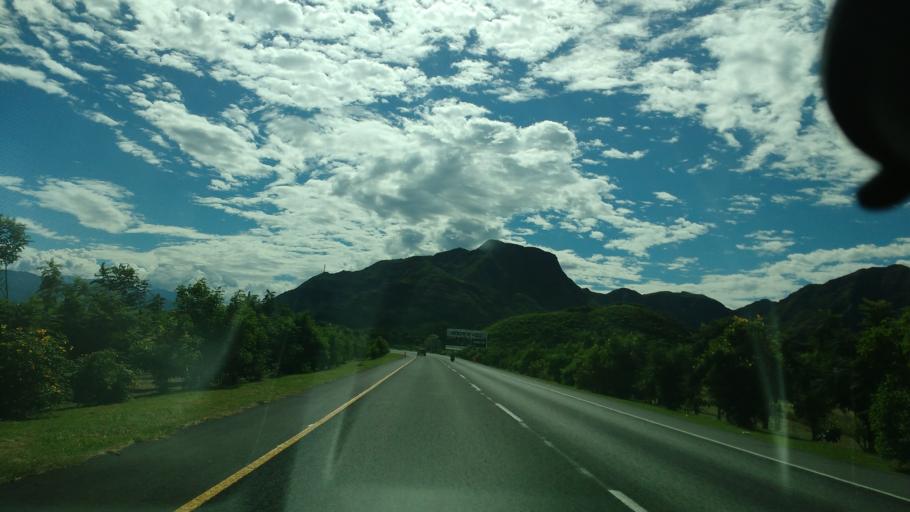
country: CO
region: Tolima
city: Valle de San Juan
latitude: 4.2765
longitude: -75.0057
